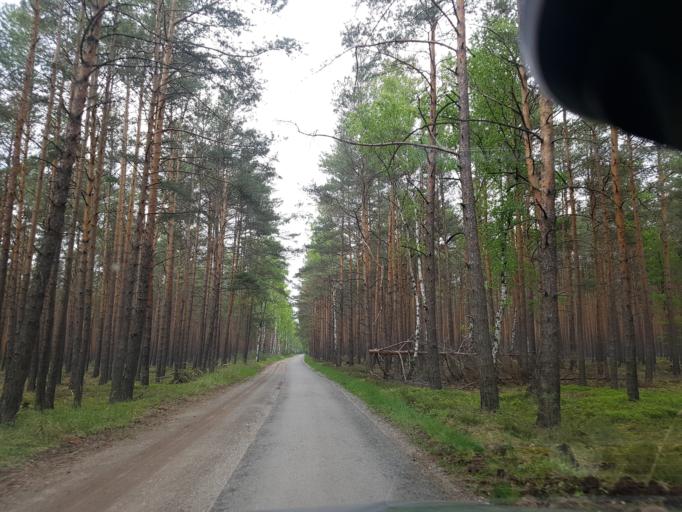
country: DE
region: Brandenburg
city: Crinitz
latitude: 51.6851
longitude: 13.7785
